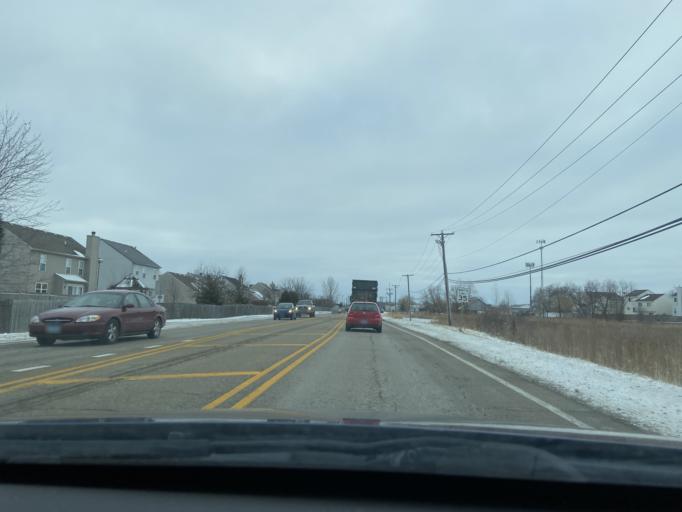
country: US
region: Illinois
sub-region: Lake County
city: Hainesville
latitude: 42.3495
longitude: -88.0673
